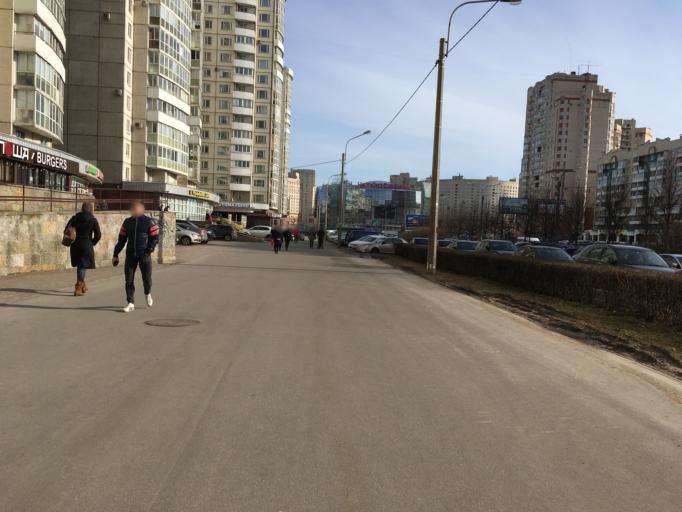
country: RU
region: St.-Petersburg
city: Komendantsky aerodrom
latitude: 60.0108
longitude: 30.2571
